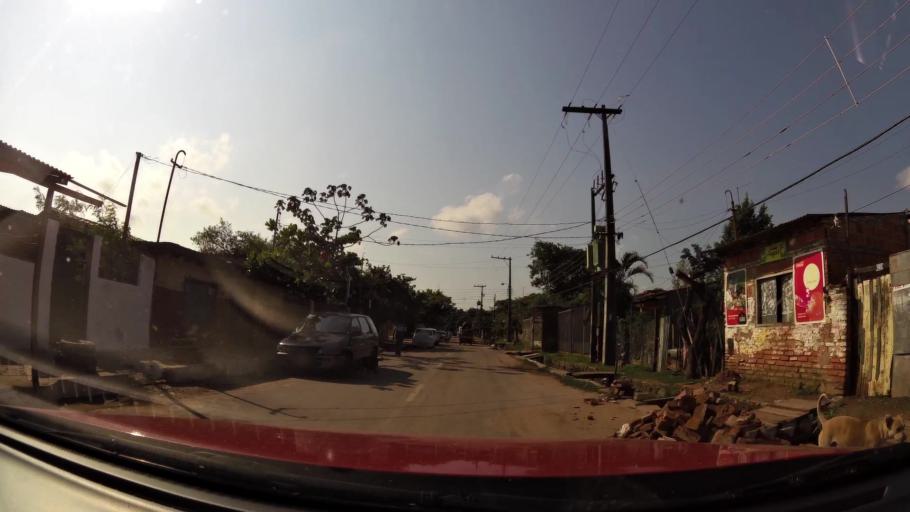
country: PY
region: Asuncion
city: Asuncion
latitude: -25.3222
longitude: -57.6427
